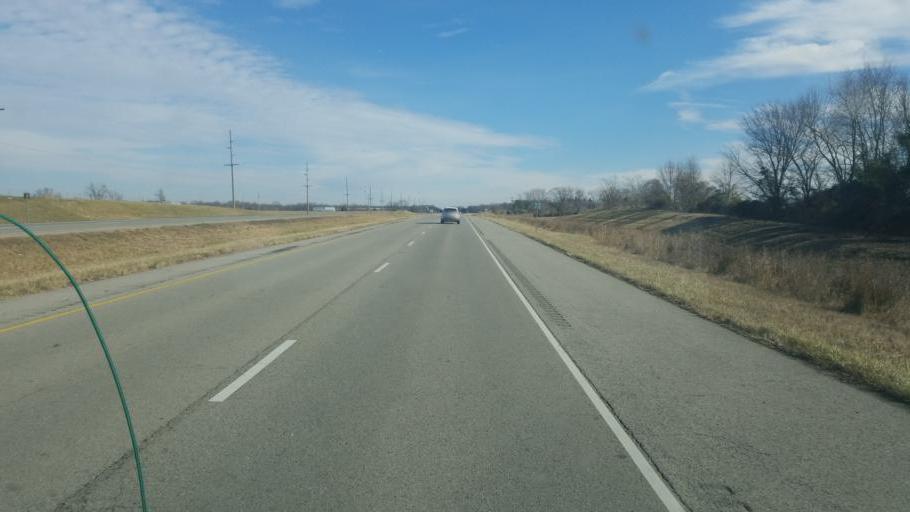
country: US
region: Illinois
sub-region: Williamson County
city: Marion
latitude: 37.7295
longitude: -88.8469
